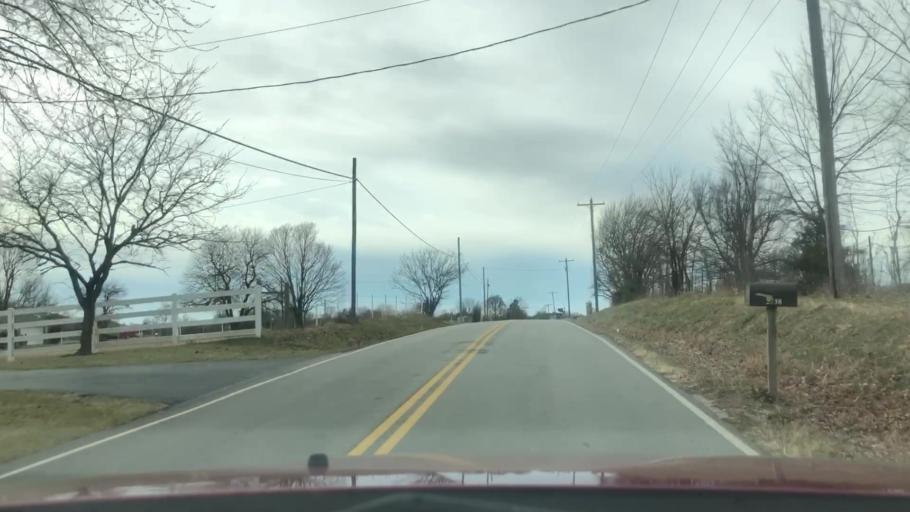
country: US
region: Missouri
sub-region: Greene County
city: Springfield
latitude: 37.2730
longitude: -93.2389
